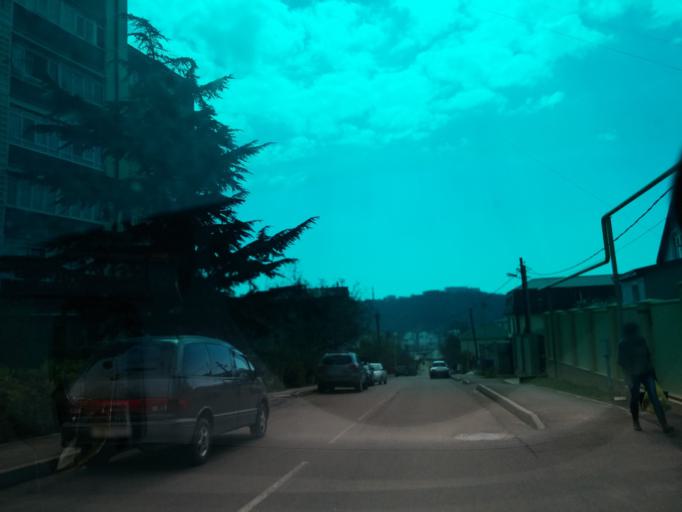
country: RU
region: Krasnodarskiy
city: Tuapse
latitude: 44.1043
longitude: 39.0849
